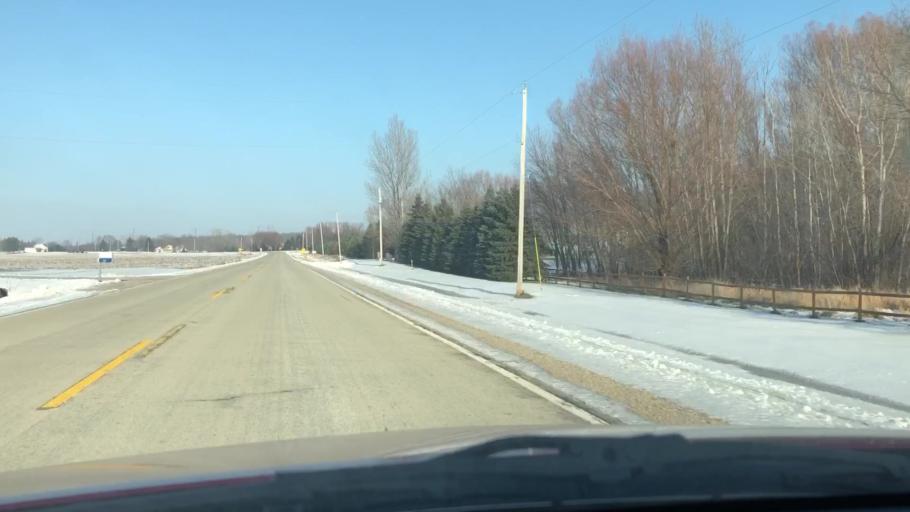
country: US
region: Wisconsin
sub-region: Outagamie County
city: Seymour
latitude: 44.4251
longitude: -88.3632
